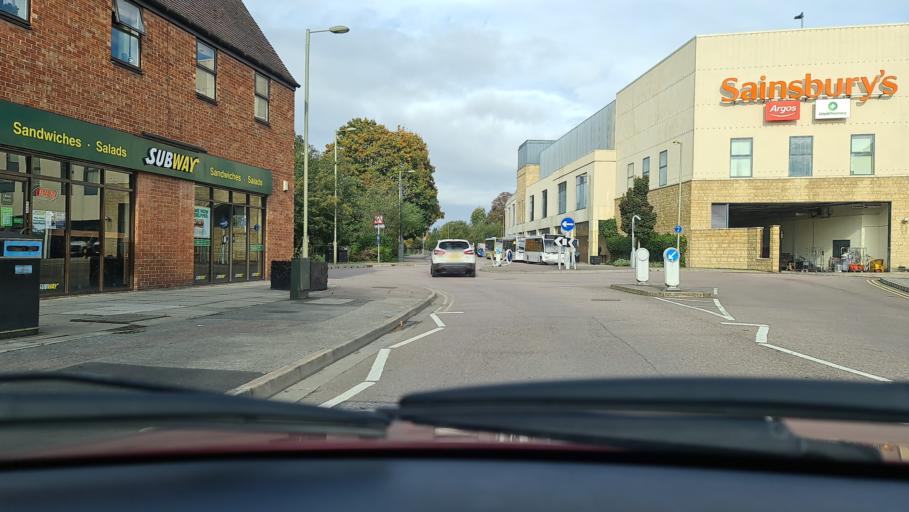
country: GB
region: England
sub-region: Oxfordshire
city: Bicester
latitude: 51.8971
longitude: -1.1522
